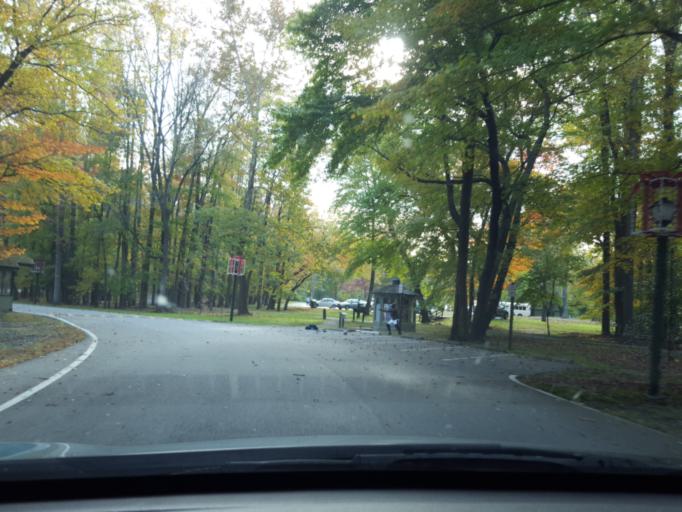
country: US
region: Maryland
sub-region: Prince George's County
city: Kettering
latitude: 38.8904
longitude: -76.7866
